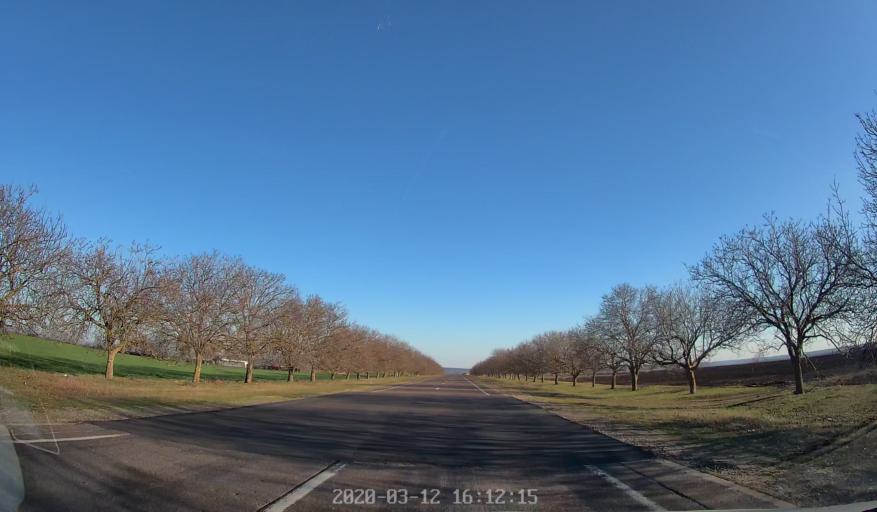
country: MD
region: Anenii Noi
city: Anenii Noi
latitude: 46.9378
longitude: 29.2702
